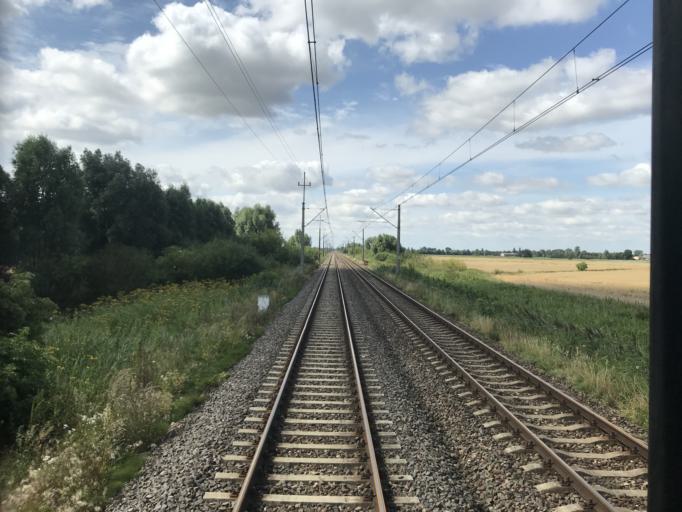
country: PL
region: Warmian-Masurian Voivodeship
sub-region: Powiat elblaski
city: Gronowo Elblaskie
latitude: 54.1202
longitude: 19.3564
